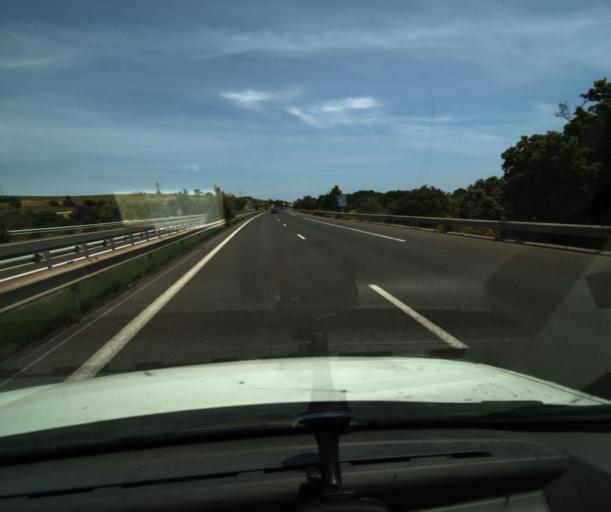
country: FR
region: Languedoc-Roussillon
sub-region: Departement des Pyrenees-Orientales
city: el Volo
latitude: 42.5320
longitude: 2.8261
